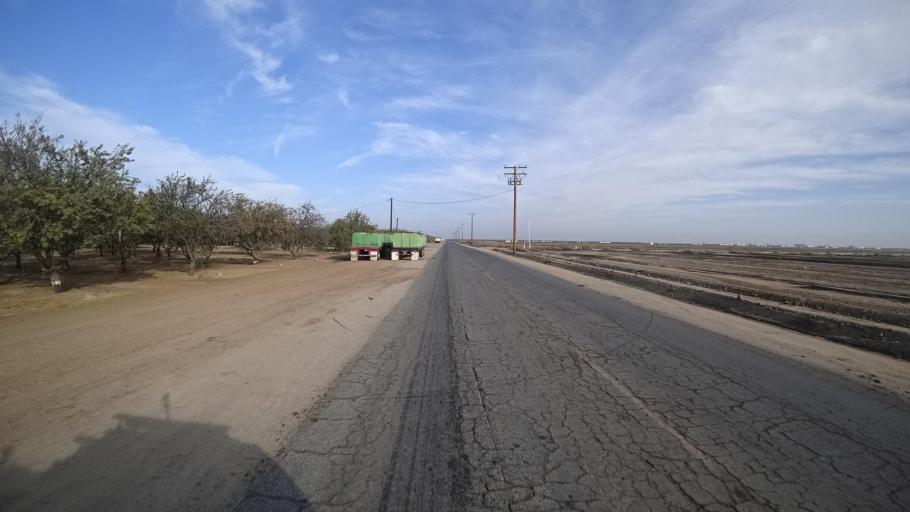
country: US
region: California
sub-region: Kern County
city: Delano
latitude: 35.7789
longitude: -119.2053
